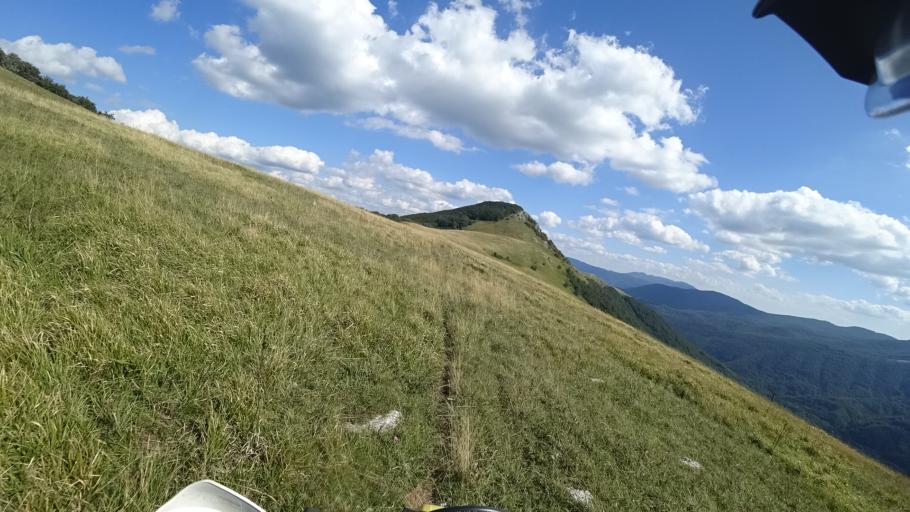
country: HR
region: Zadarska
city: Gracac
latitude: 44.3872
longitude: 16.0402
